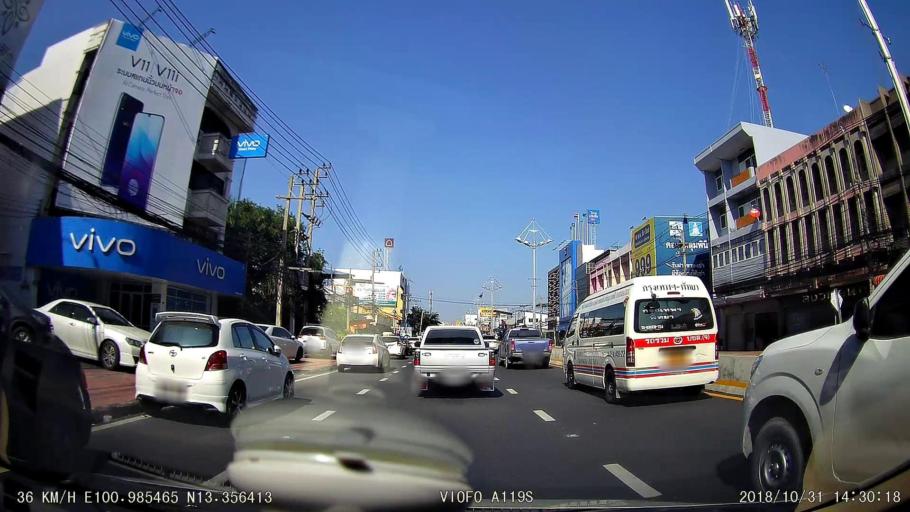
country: TH
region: Chon Buri
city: Chon Buri
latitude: 13.3565
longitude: 100.9855
